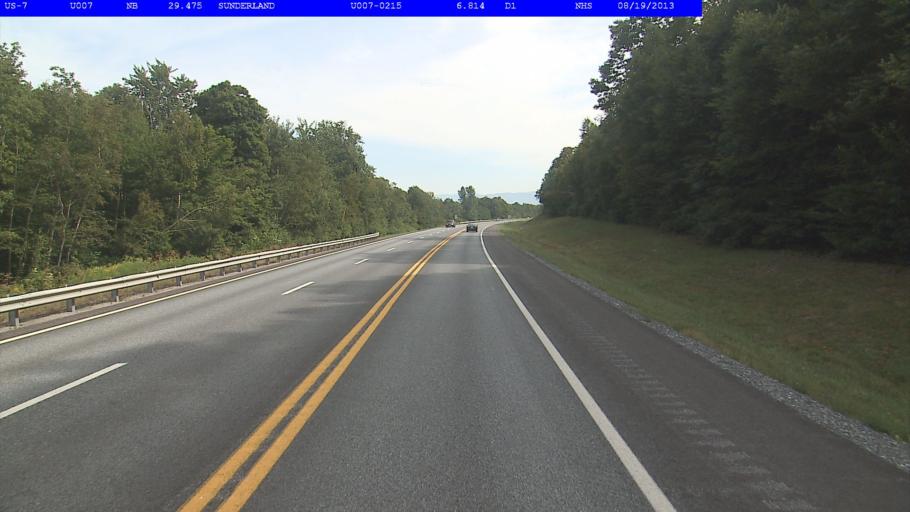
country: US
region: Vermont
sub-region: Bennington County
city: Manchester Center
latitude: 43.1147
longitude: -73.0862
